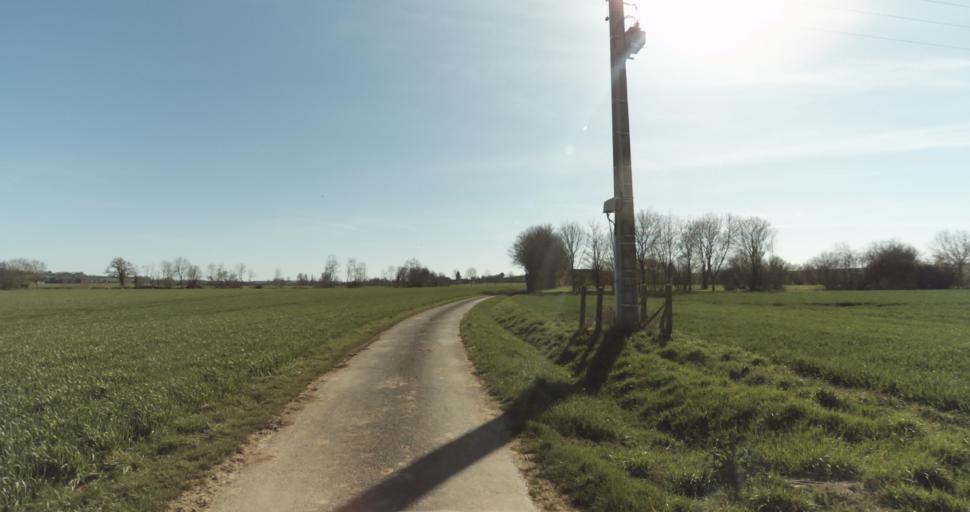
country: FR
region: Lower Normandy
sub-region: Departement du Calvados
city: Saint-Pierre-sur-Dives
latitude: 49.0266
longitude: 0.0203
